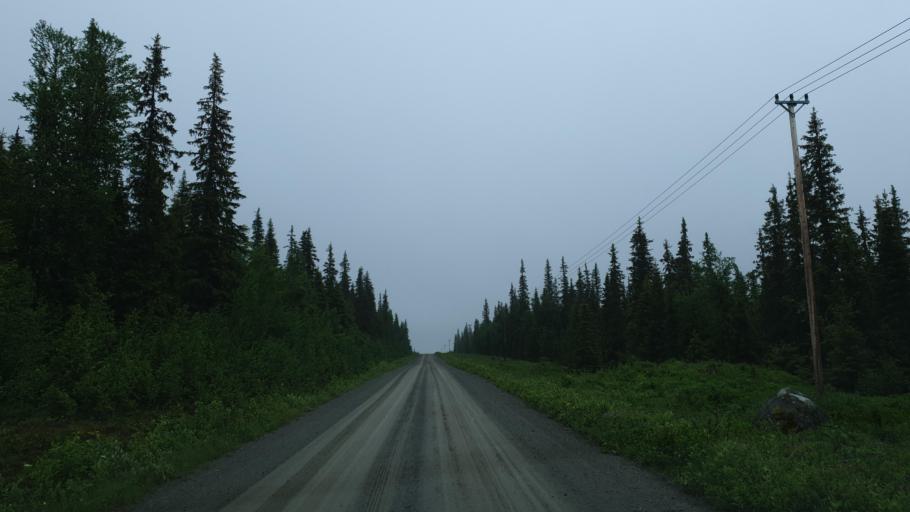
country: SE
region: Vaesterbotten
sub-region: Vilhelmina Kommun
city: Sjoberg
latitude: 65.3186
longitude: 15.9462
